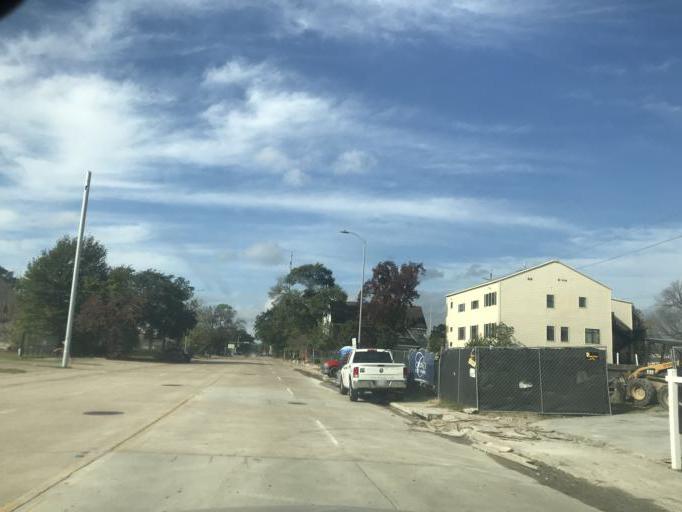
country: US
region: Texas
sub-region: Harris County
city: Bellaire
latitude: 29.7355
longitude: -95.4815
